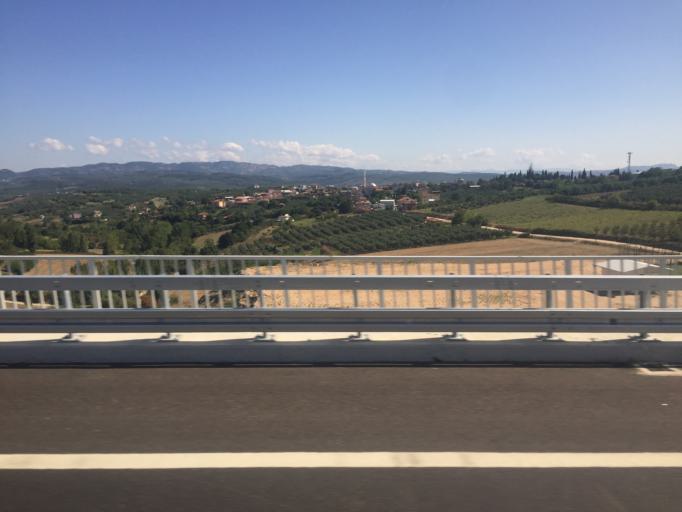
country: TR
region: Bursa
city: Gorukle
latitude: 40.2491
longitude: 28.7512
